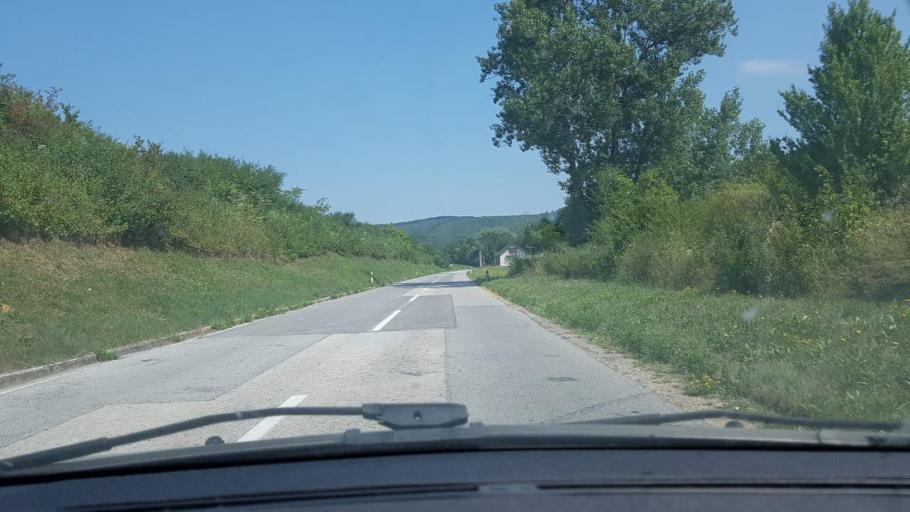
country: BA
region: Federation of Bosnia and Herzegovina
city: Velika Kladusa
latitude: 45.2326
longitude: 15.7349
